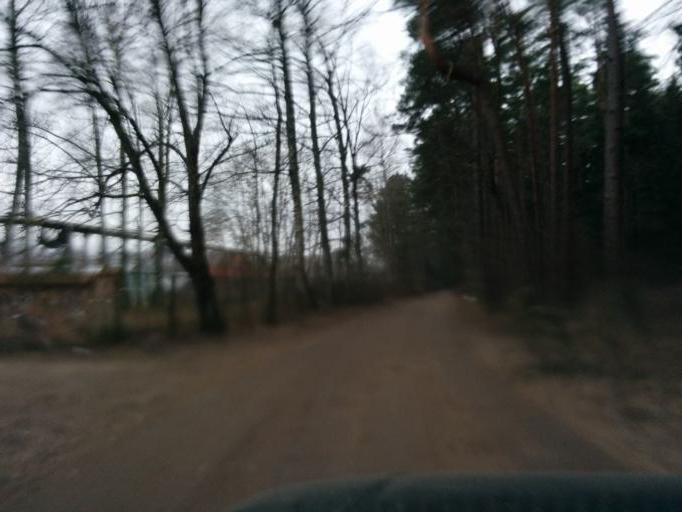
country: LV
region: Babite
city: Pinki
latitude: 56.9710
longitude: 23.8453
